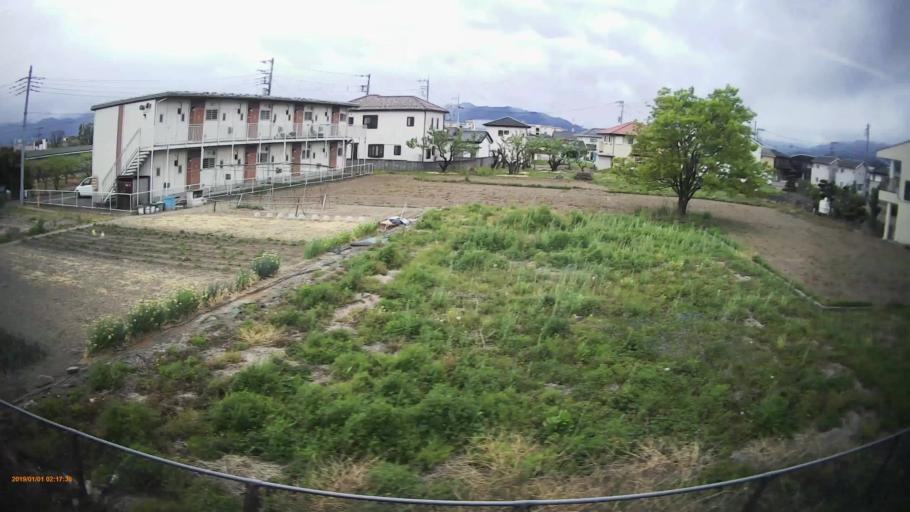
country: JP
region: Yamanashi
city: Kofu-shi
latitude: 35.6691
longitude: 138.5321
